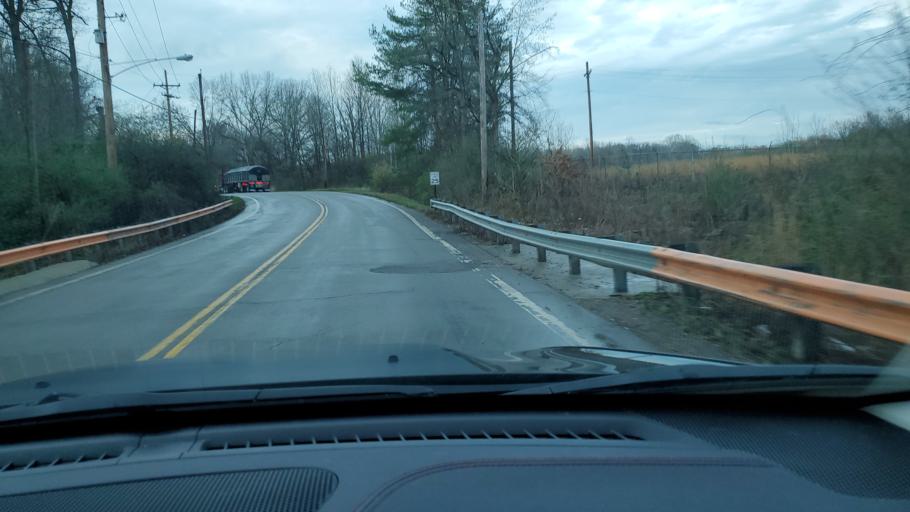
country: US
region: Ohio
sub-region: Trumbull County
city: Niles
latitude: 41.1677
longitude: -80.7544
